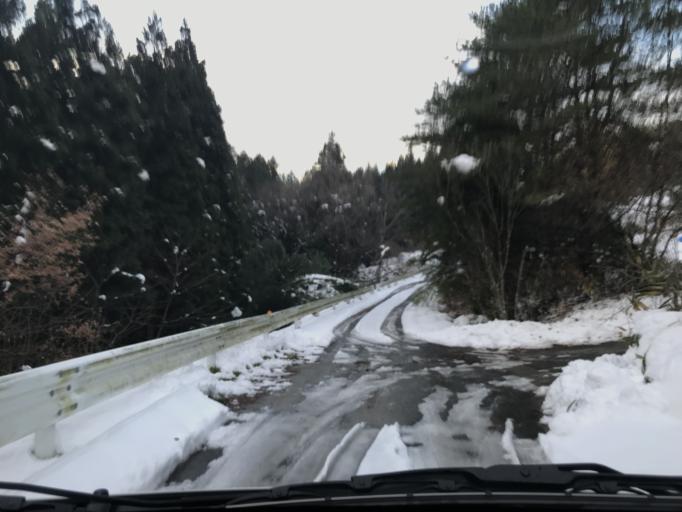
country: JP
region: Iwate
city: Mizusawa
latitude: 39.0485
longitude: 141.0524
